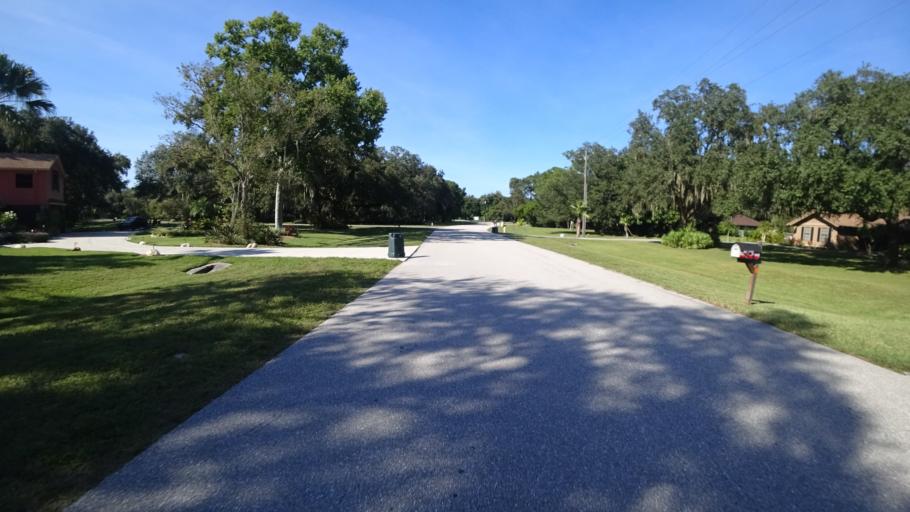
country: US
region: Florida
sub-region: Sarasota County
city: The Meadows
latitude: 27.4203
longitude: -82.4477
